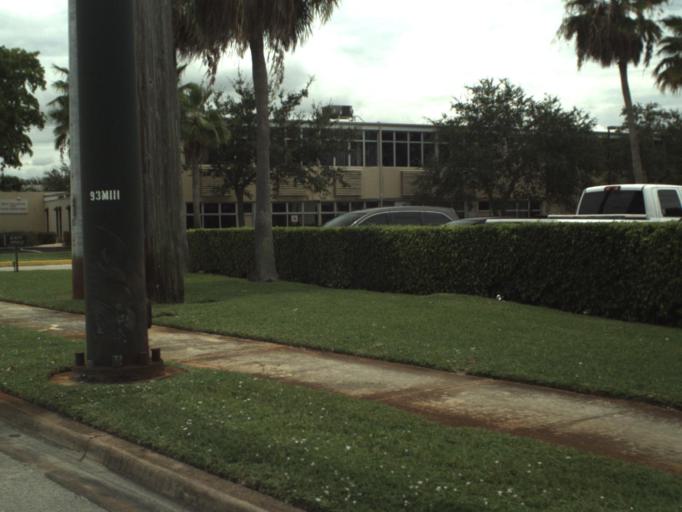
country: US
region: Florida
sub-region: Palm Beach County
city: Lake Park
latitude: 26.8119
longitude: -80.0569
